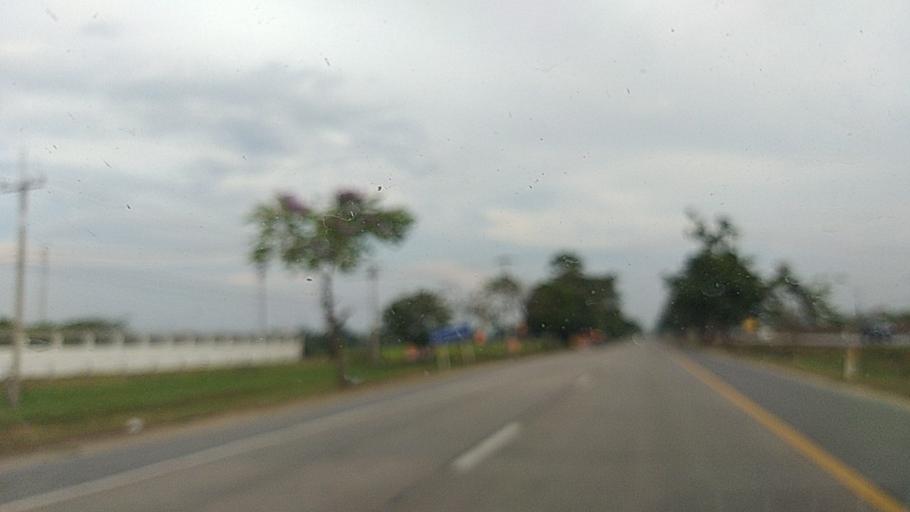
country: TH
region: Phra Nakhon Si Ayutthaya
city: Bang Pa-in
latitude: 14.2812
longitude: 100.5277
